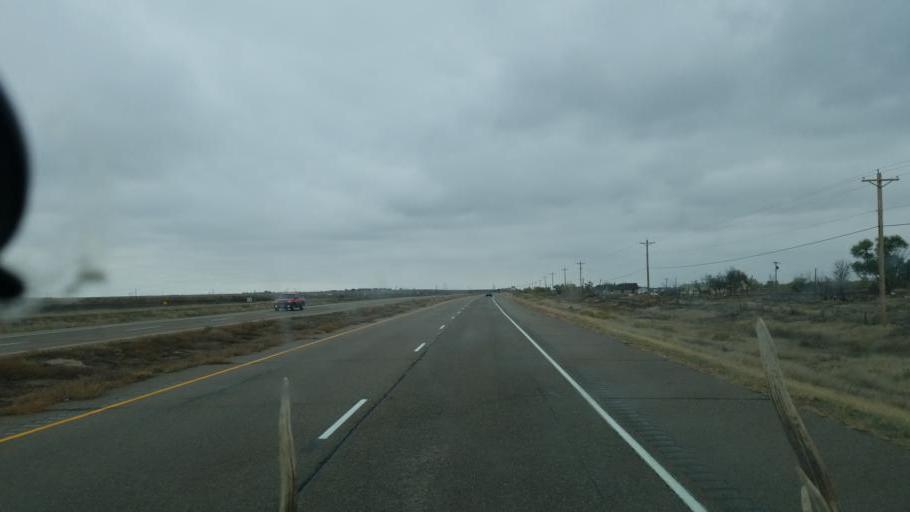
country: US
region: Colorado
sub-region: Pueblo County
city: Pueblo
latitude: 38.2705
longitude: -104.4126
